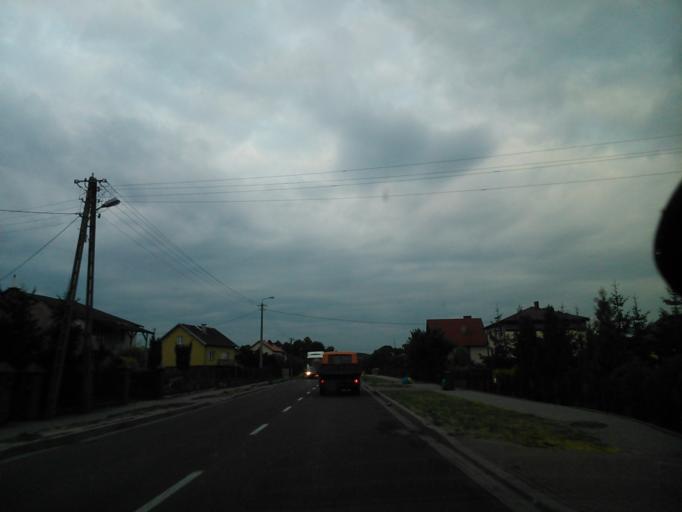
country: PL
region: Masovian Voivodeship
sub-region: Powiat mlawski
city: Lipowiec Koscielny
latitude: 53.1065
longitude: 20.1890
